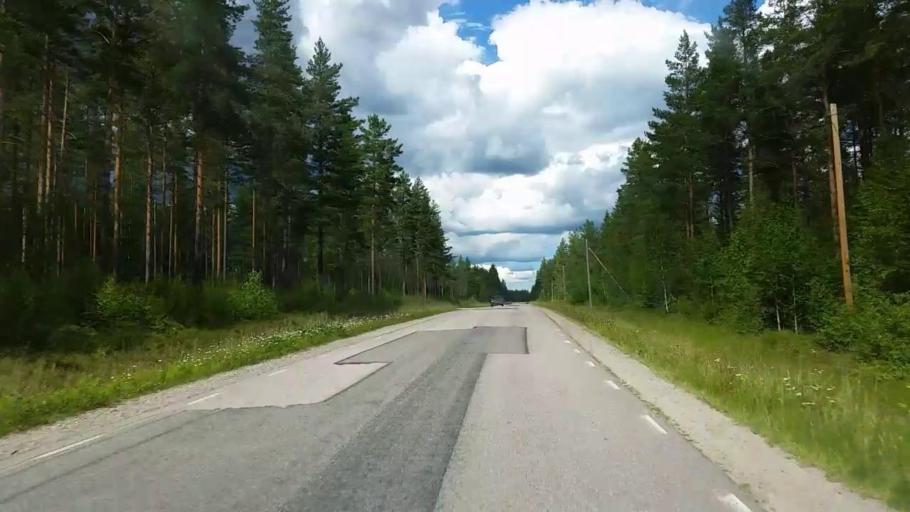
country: SE
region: Gaevleborg
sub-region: Ovanakers Kommun
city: Edsbyn
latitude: 61.4020
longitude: 15.8961
